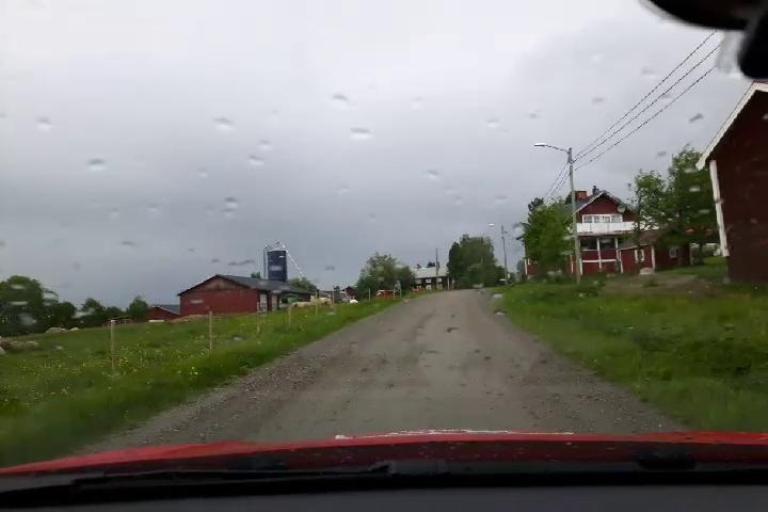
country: SE
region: Jaemtland
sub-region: Bergs Kommun
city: Hoverberg
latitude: 62.7375
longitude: 14.4555
